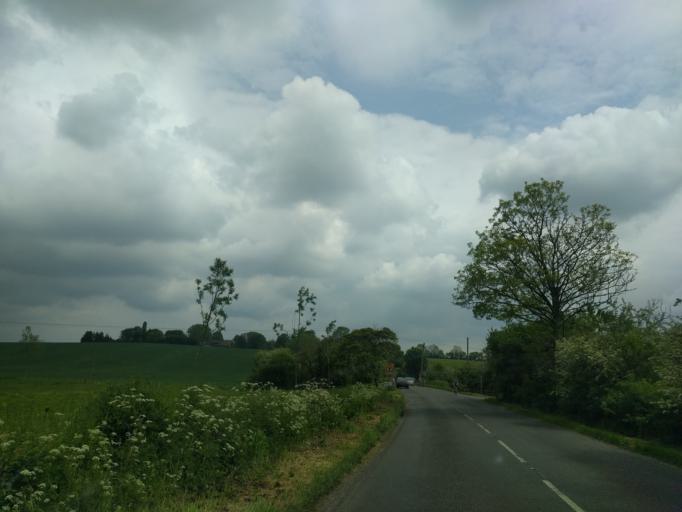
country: GB
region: England
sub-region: Somerset
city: Langport
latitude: 51.0443
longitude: -2.8002
